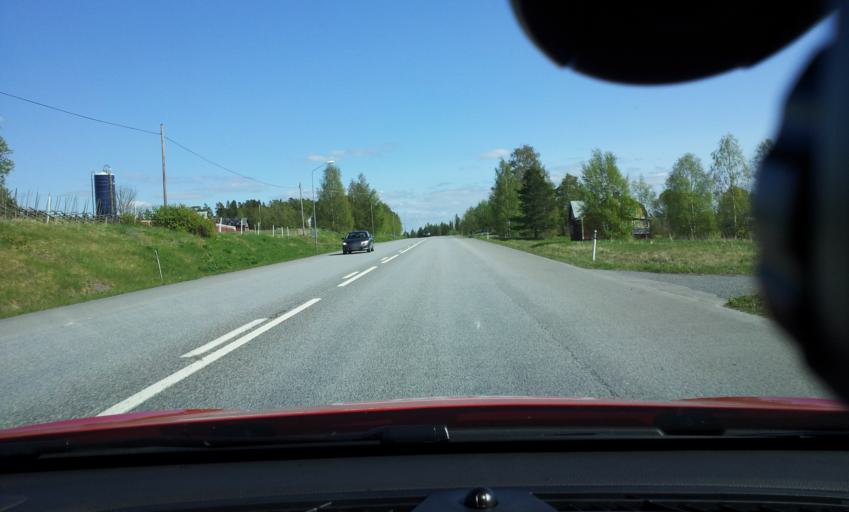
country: SE
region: Jaemtland
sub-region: Krokoms Kommun
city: Krokom
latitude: 63.3168
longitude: 14.0898
